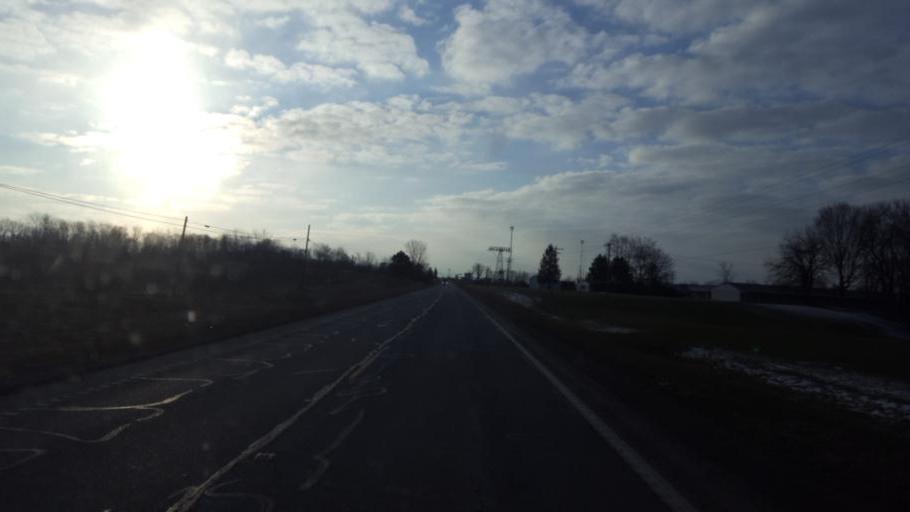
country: US
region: Ohio
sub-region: Morrow County
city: Mount Gilead
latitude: 40.5030
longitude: -82.7296
